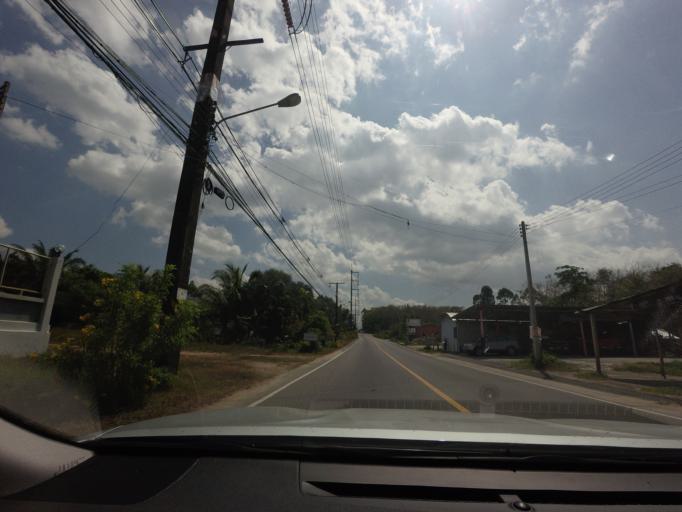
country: TH
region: Phangnga
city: Thai Mueang
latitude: 8.3966
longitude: 98.2613
